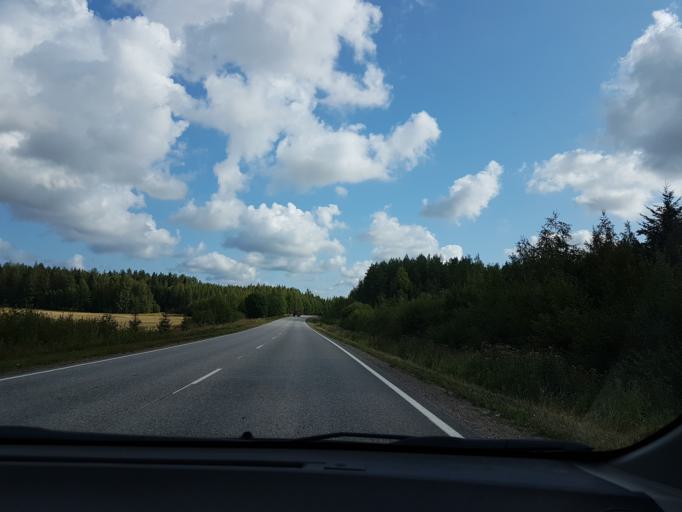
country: FI
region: Uusimaa
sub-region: Helsinki
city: Pornainen
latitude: 60.4692
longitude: 25.2953
